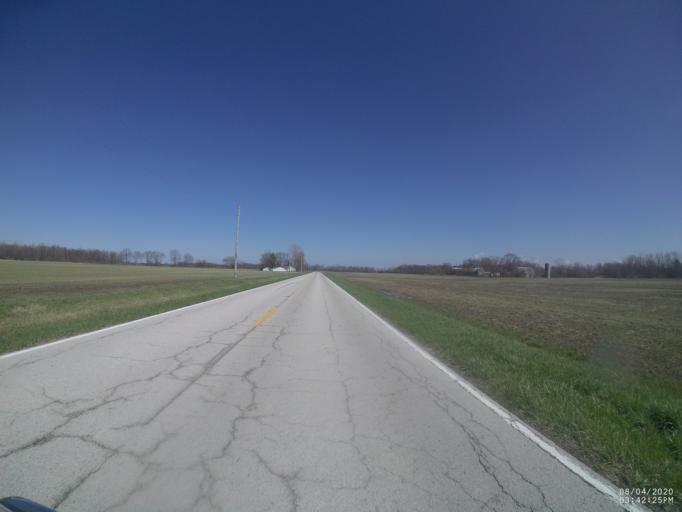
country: US
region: Ohio
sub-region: Sandusky County
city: Ballville
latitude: 41.2527
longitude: -83.2321
